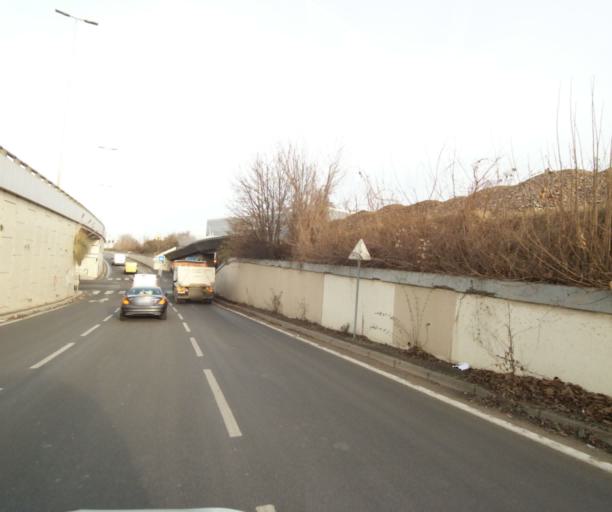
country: FR
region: Ile-de-France
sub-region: Departement des Hauts-de-Seine
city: Nanterre
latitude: 48.9037
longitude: 2.2193
